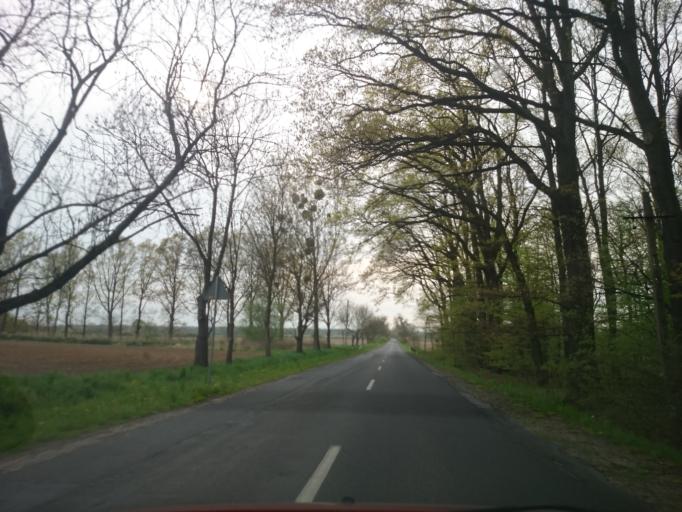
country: PL
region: Opole Voivodeship
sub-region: Powiat nyski
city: Sidzina
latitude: 50.6405
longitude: 17.5068
